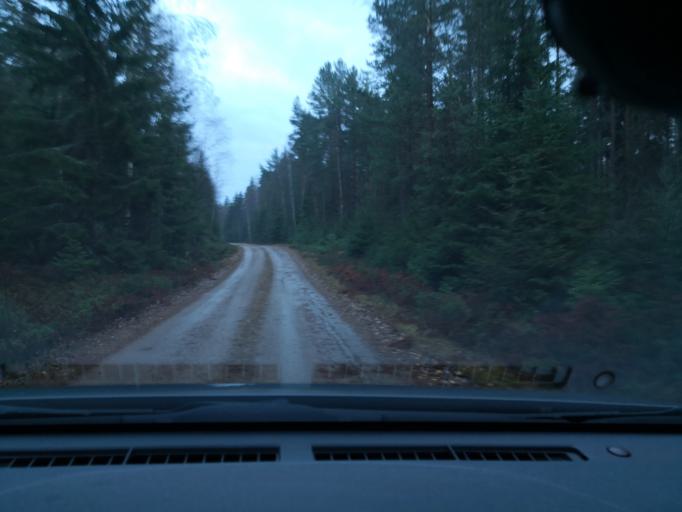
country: SE
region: Vaestmanland
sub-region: Hallstahammars Kommun
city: Hallstahammar
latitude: 59.5586
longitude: 16.1570
